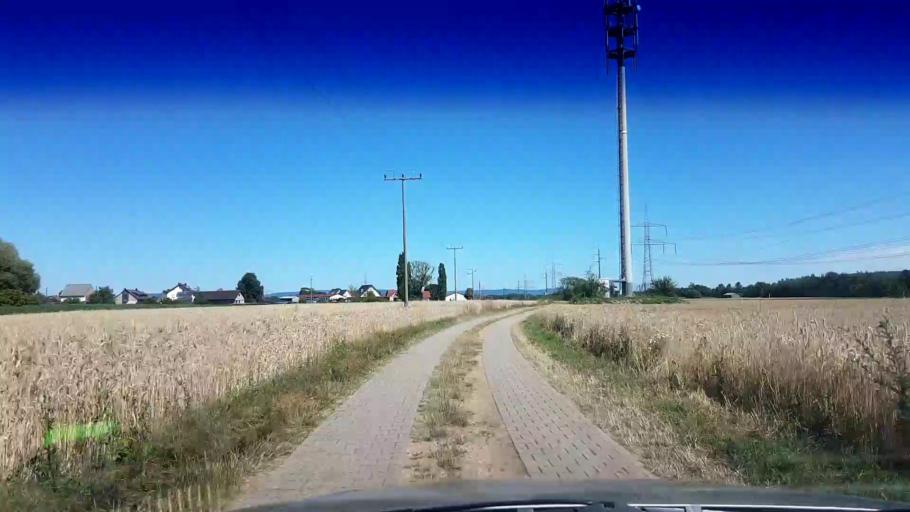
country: DE
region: Bavaria
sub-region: Upper Franconia
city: Oberhaid
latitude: 49.9310
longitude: 10.8095
